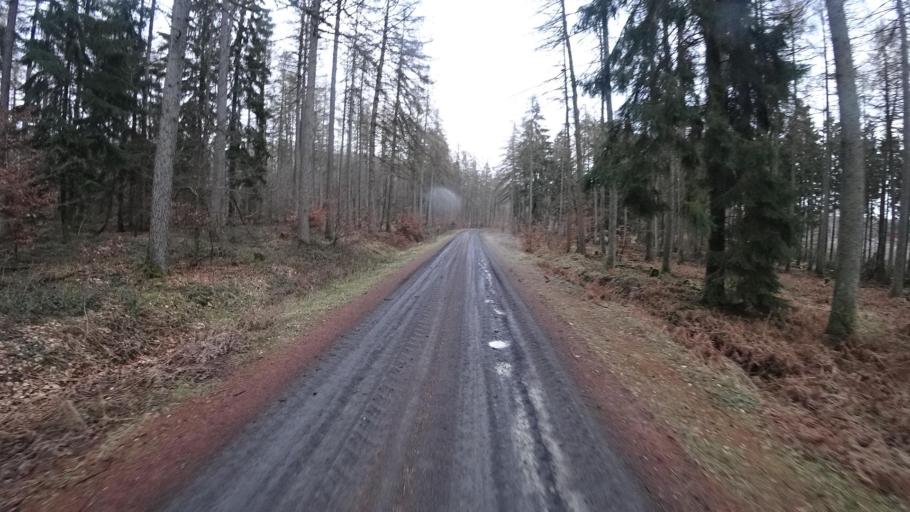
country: DE
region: Rheinland-Pfalz
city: Arzbach
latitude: 50.4086
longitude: 7.7543
